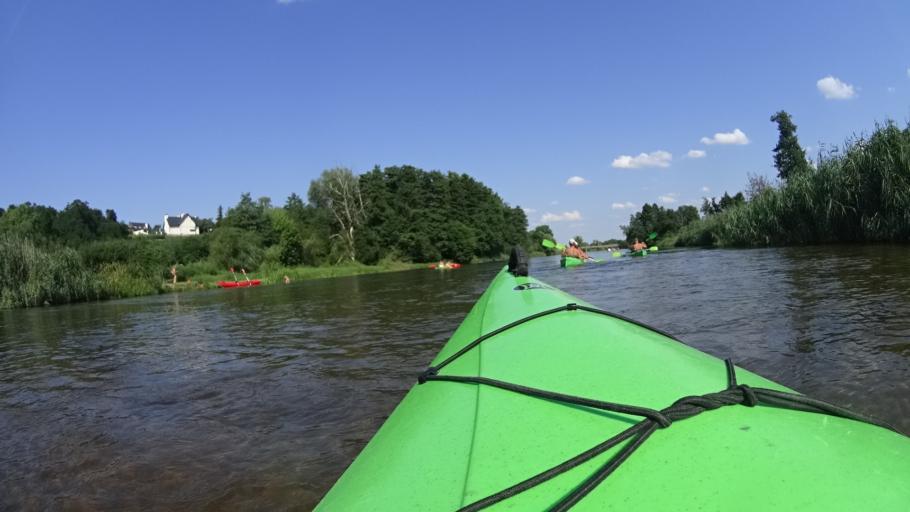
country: PL
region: Masovian Voivodeship
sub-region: Powiat bialobrzeski
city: Bialobrzegi
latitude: 51.6654
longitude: 20.9124
